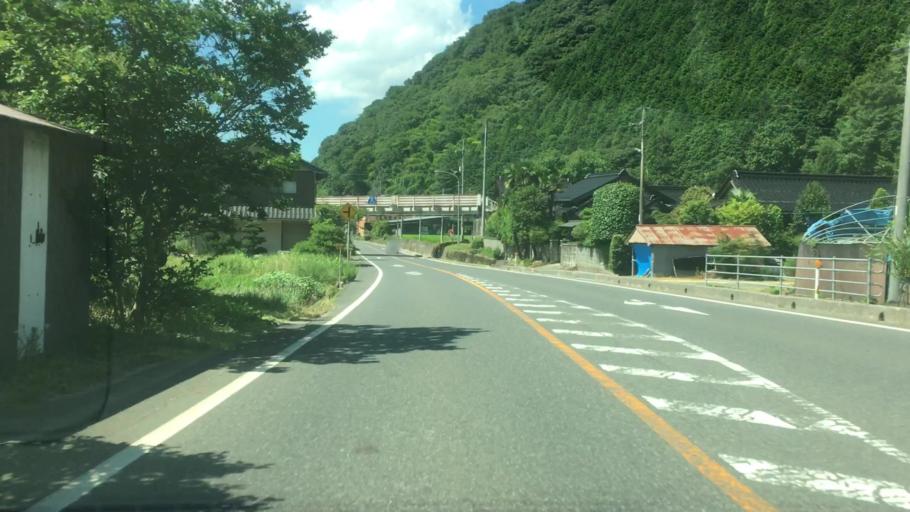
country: JP
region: Tottori
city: Tottori
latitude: 35.2535
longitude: 134.2298
